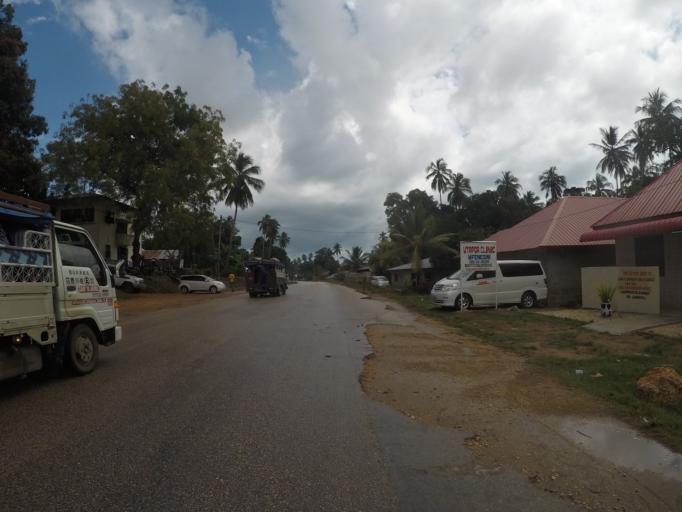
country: TZ
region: Zanzibar Central/South
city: Koani
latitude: -6.0426
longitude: 39.2286
